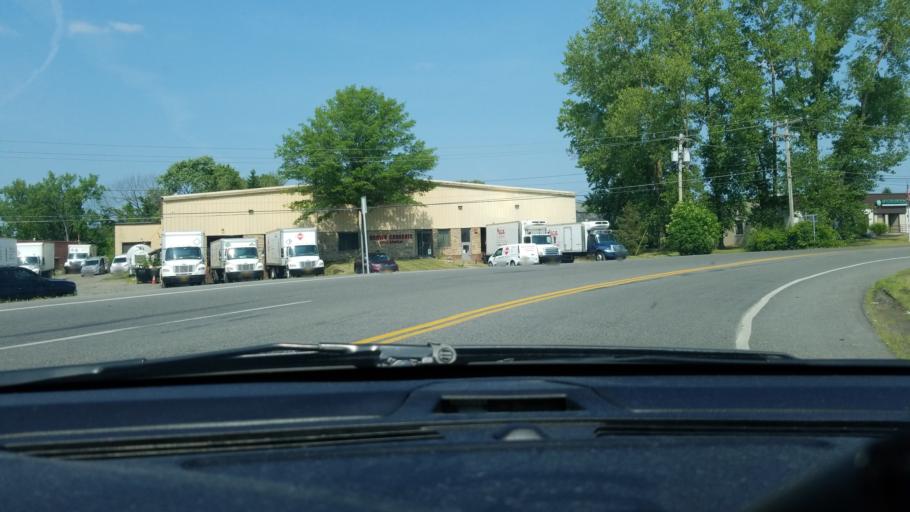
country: US
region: New York
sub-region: Onondaga County
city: East Syracuse
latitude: 43.0982
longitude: -76.0788
